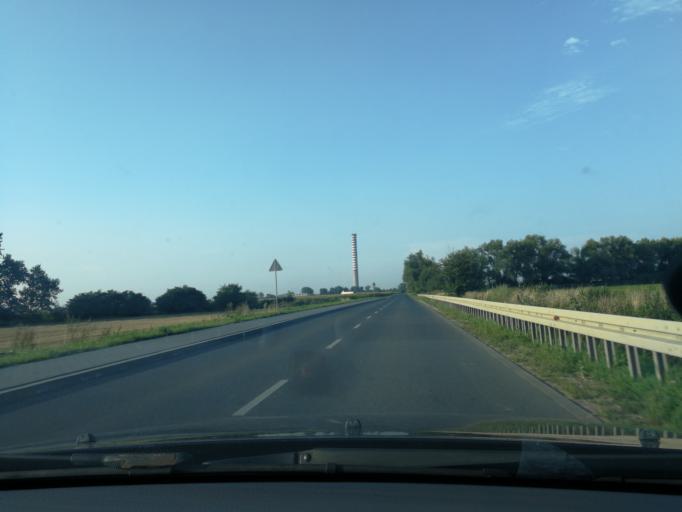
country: PL
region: Masovian Voivodeship
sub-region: Powiat pruszkowski
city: Brwinow
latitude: 52.1571
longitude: 20.7320
